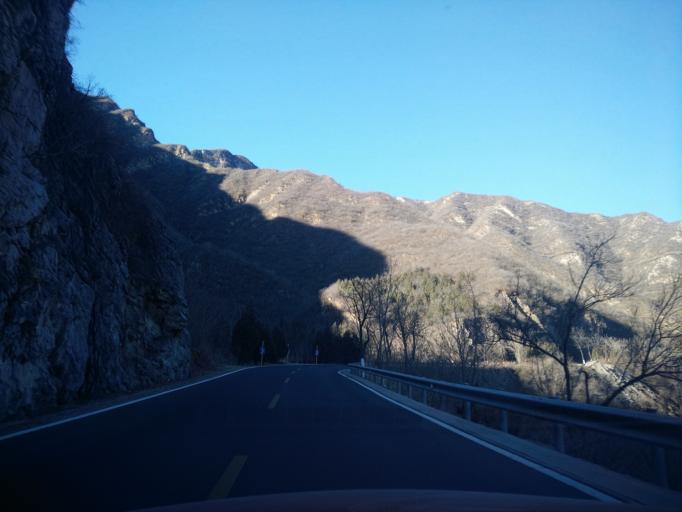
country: CN
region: Beijing
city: Wangping
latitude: 40.0047
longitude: 115.9843
